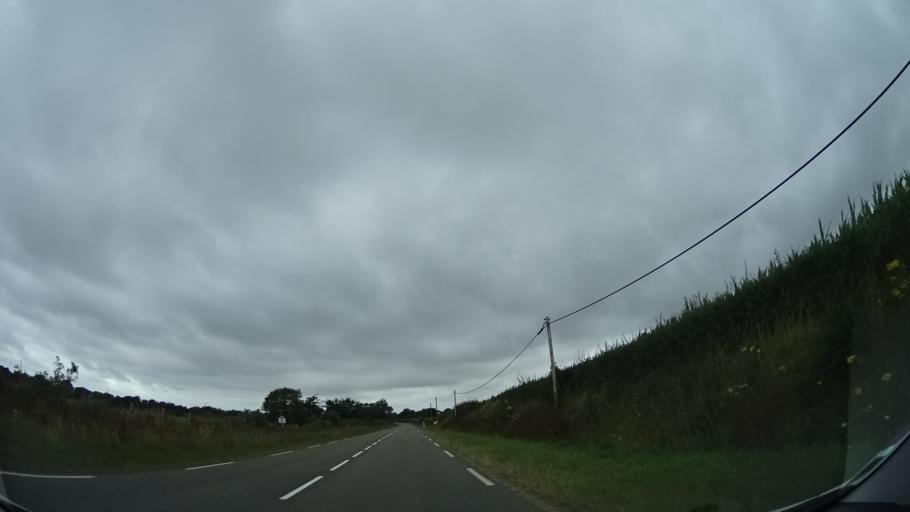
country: FR
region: Lower Normandy
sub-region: Departement de la Manche
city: La Haye-du-Puits
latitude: 49.3093
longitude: -1.5978
